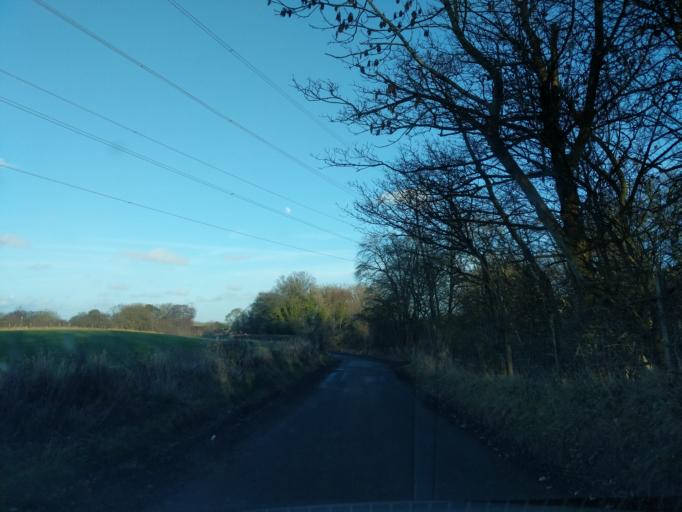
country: GB
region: Scotland
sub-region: West Lothian
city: Kirknewton
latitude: 55.8914
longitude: -3.3938
